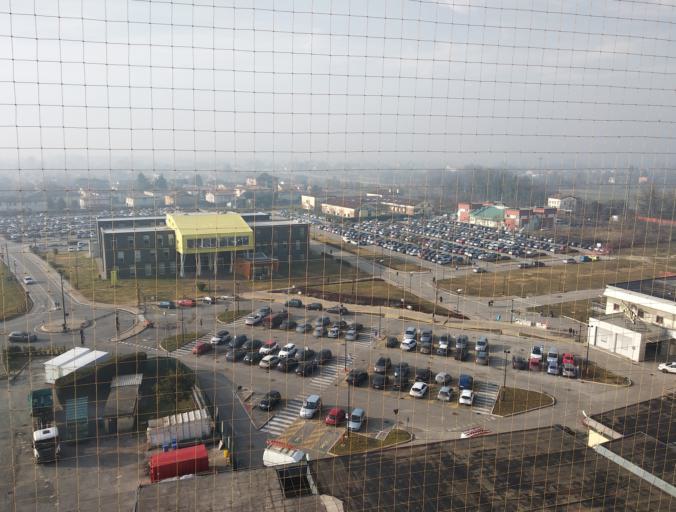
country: IT
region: Veneto
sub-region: Provincia di Padova
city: Camposampiero
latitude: 45.5643
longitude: 11.9296
